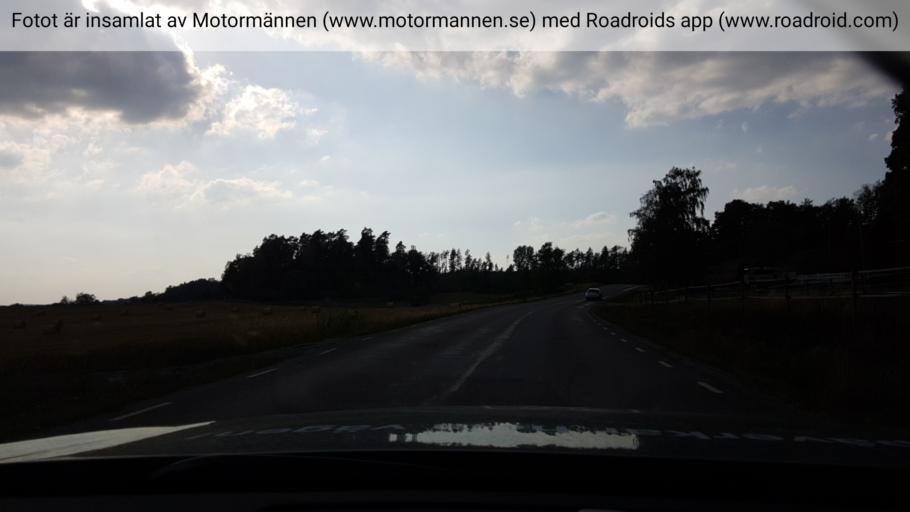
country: SE
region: Soedermanland
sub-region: Gnesta Kommun
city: Gnesta
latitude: 59.0800
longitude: 17.2716
